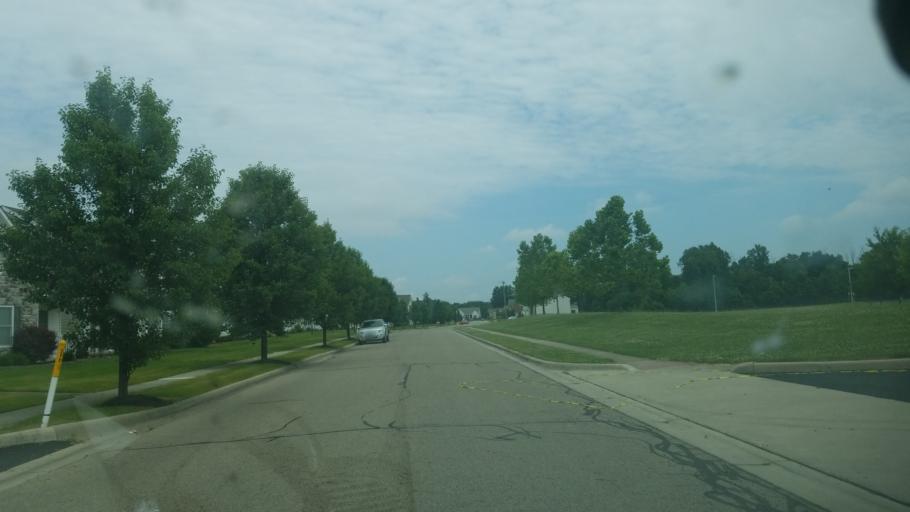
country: US
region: Ohio
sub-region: Franklin County
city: Reynoldsburg
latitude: 40.0121
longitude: -82.7828
